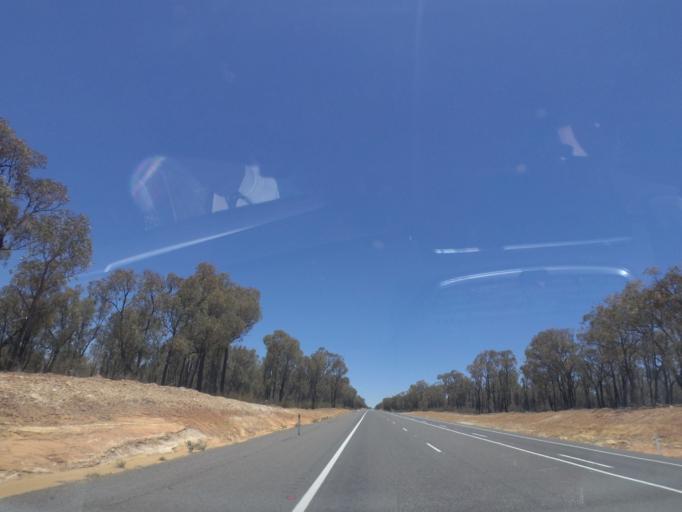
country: AU
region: New South Wales
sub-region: Warrumbungle Shire
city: Coonabarabran
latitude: -30.8958
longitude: 149.4409
